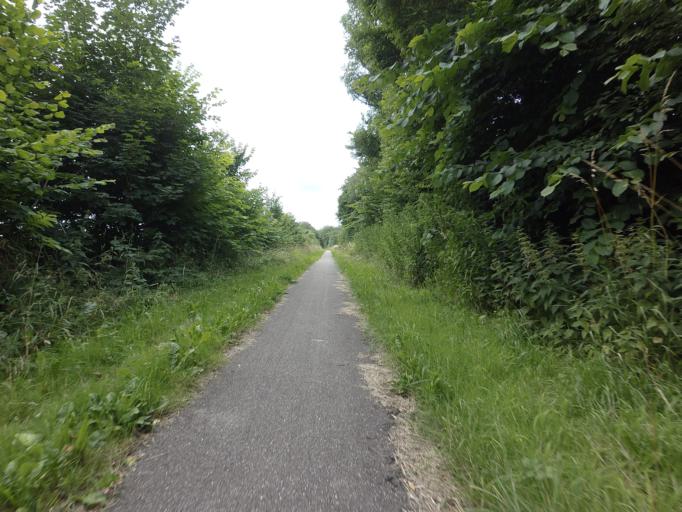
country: DK
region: Central Jutland
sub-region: Randers Kommune
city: Langa
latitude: 56.3332
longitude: 9.9011
